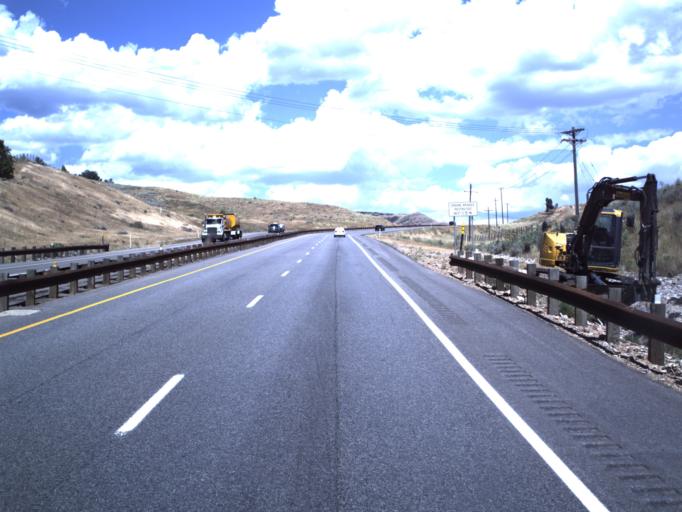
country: US
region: Utah
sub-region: Wasatch County
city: Midway
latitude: 40.3848
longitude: -111.5517
